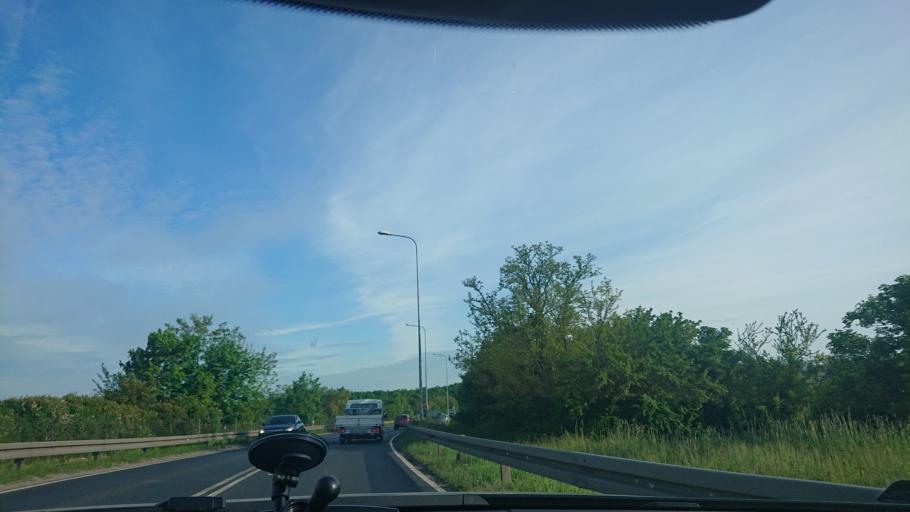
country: PL
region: Greater Poland Voivodeship
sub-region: Powiat gnieznienski
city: Gniezno
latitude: 52.5261
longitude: 17.5855
